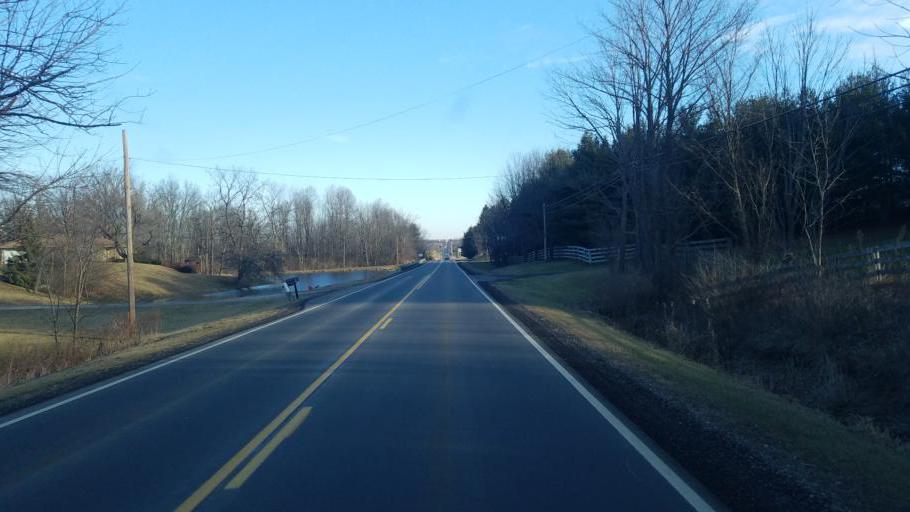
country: US
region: Ohio
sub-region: Morrow County
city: Mount Gilead
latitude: 40.5333
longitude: -82.8323
